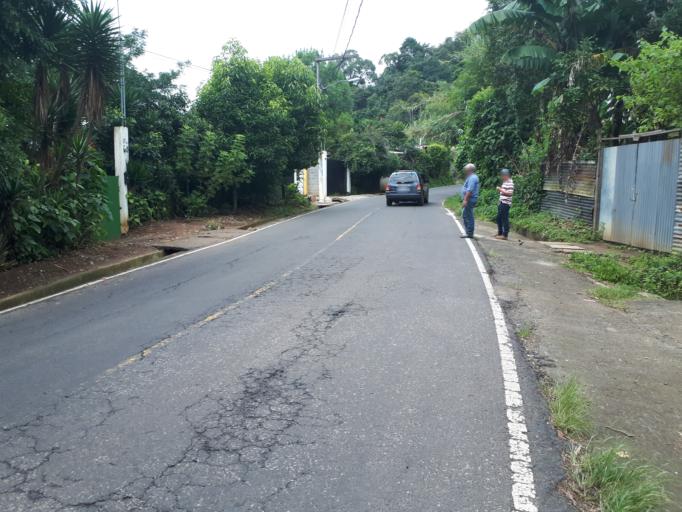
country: GT
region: Guatemala
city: Villa Canales
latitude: 14.4558
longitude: -90.5074
